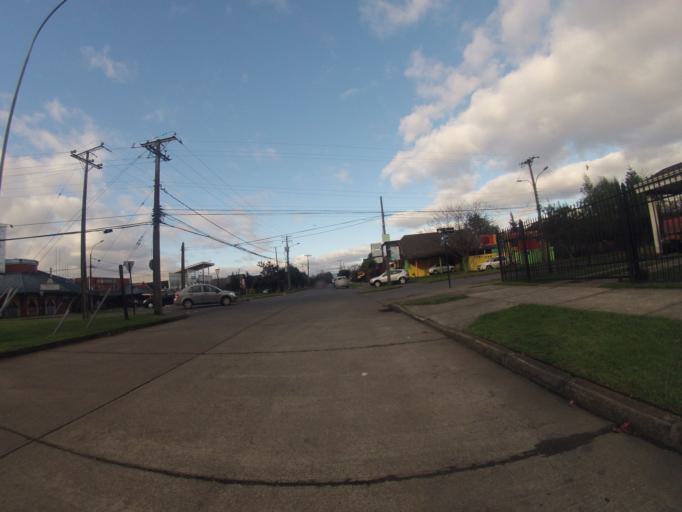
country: CL
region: Araucania
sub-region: Provincia de Cautin
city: Temuco
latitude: -38.7361
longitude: -72.6402
